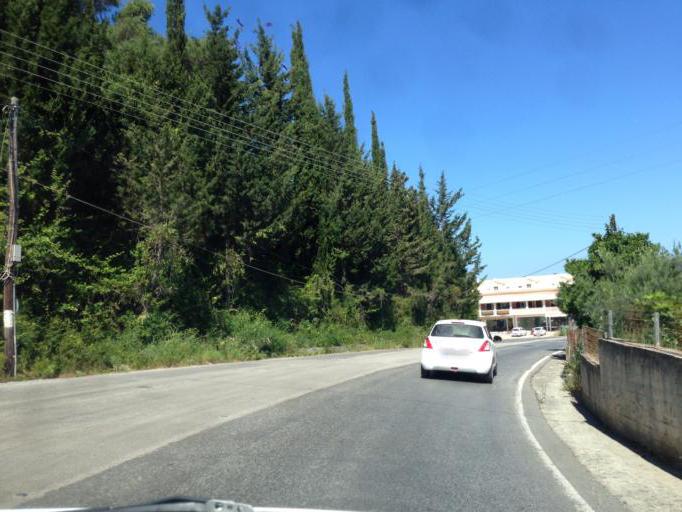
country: GR
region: Ionian Islands
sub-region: Nomos Kerkyras
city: Agios Georgis
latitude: 39.7858
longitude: 19.7413
